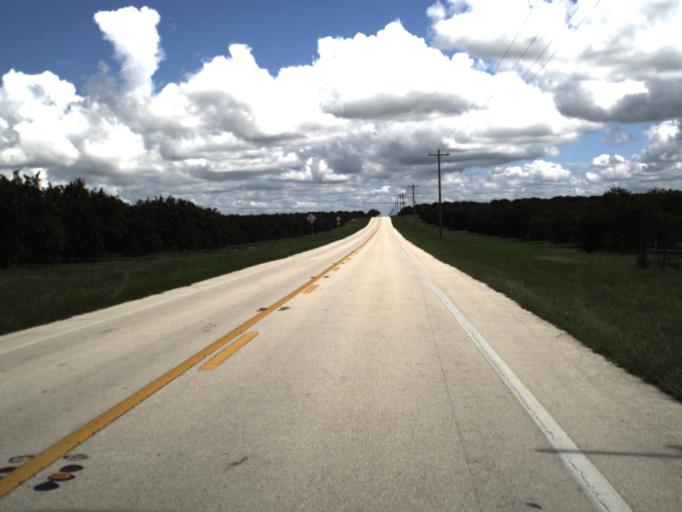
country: US
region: Florida
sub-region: Polk County
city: Fort Meade
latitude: 27.7335
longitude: -81.7243
